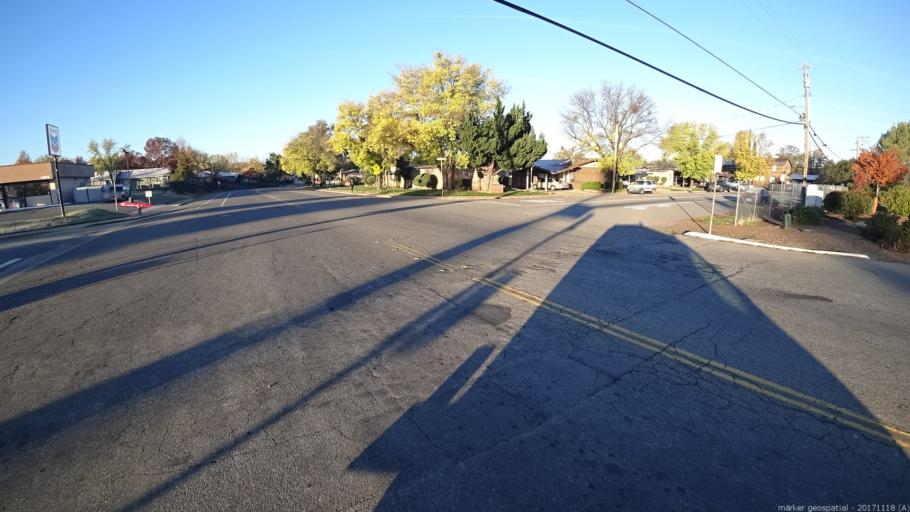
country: US
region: California
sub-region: Shasta County
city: Anderson
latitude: 40.4385
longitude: -122.2915
